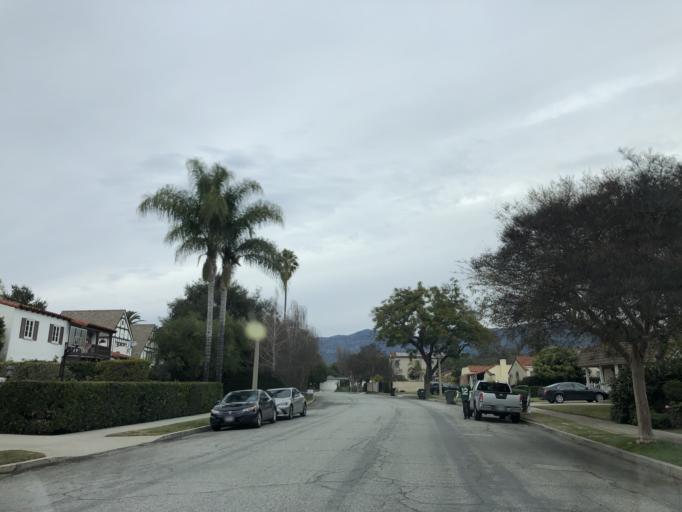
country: US
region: California
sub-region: Los Angeles County
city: San Gabriel
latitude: 34.1084
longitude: -118.1074
